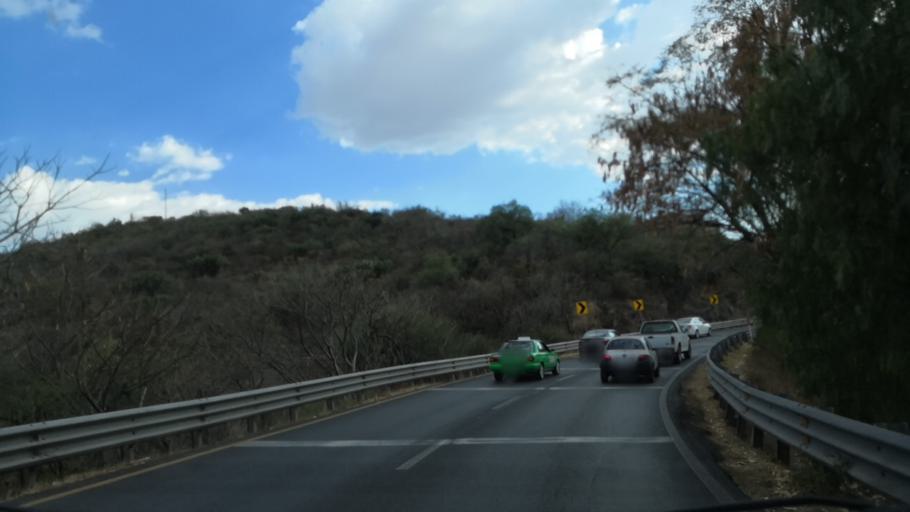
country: MX
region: Guanajuato
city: Marfil
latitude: 20.9990
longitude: -101.2846
